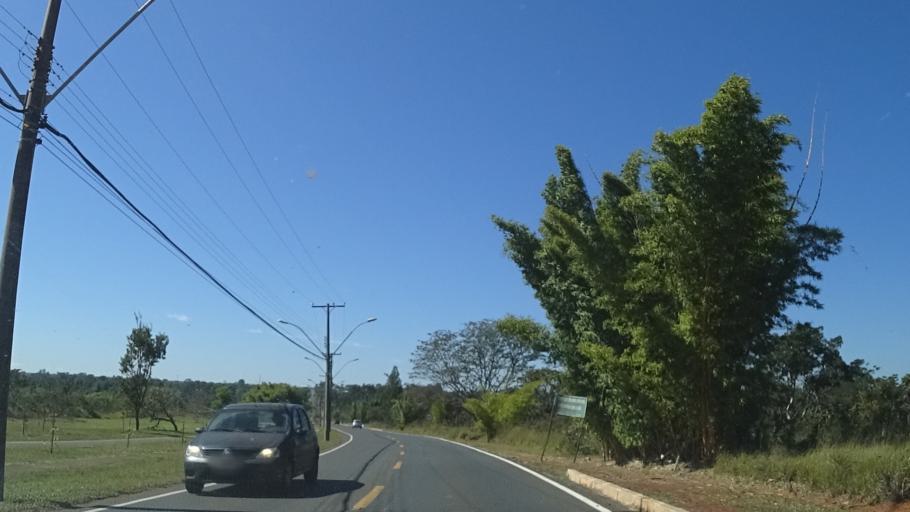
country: BR
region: Federal District
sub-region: Brasilia
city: Brasilia
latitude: -15.8949
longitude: -47.9467
